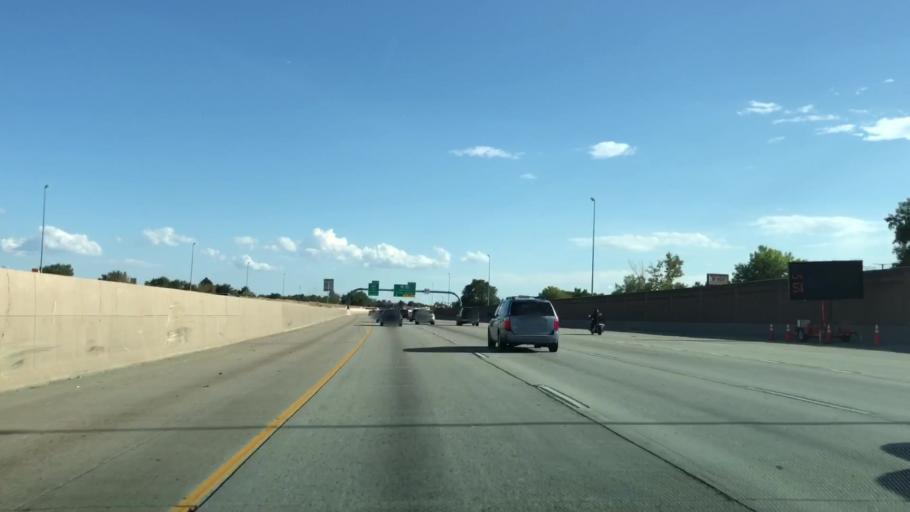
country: US
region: Colorado
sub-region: Adams County
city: Aurora
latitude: 39.7520
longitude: -104.8272
